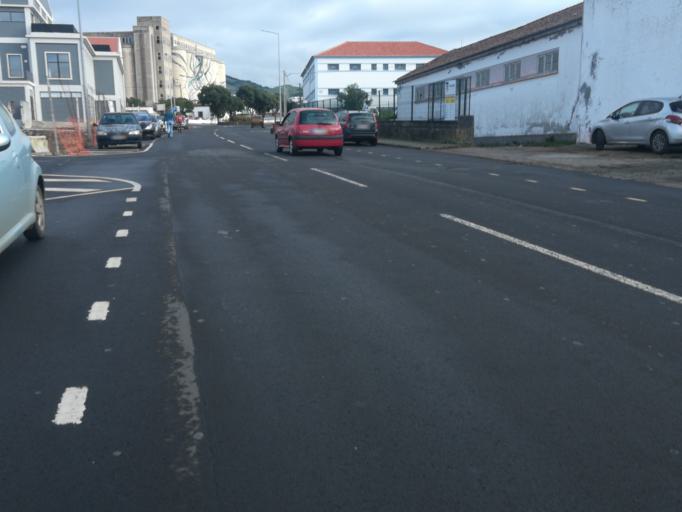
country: PT
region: Azores
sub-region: Angra do Heroismo
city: Angra do Heroismo
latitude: 38.6530
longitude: -27.2134
